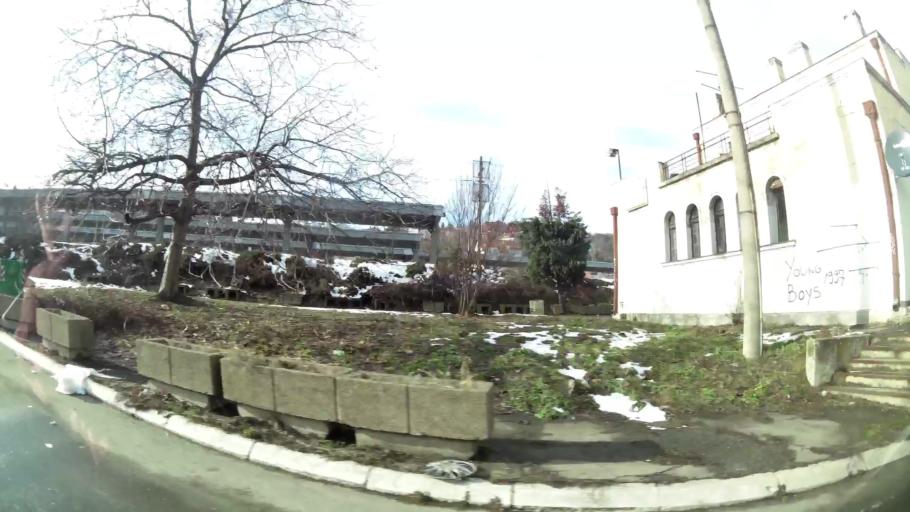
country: RS
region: Central Serbia
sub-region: Belgrade
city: Rakovica
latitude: 44.7471
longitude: 20.4439
